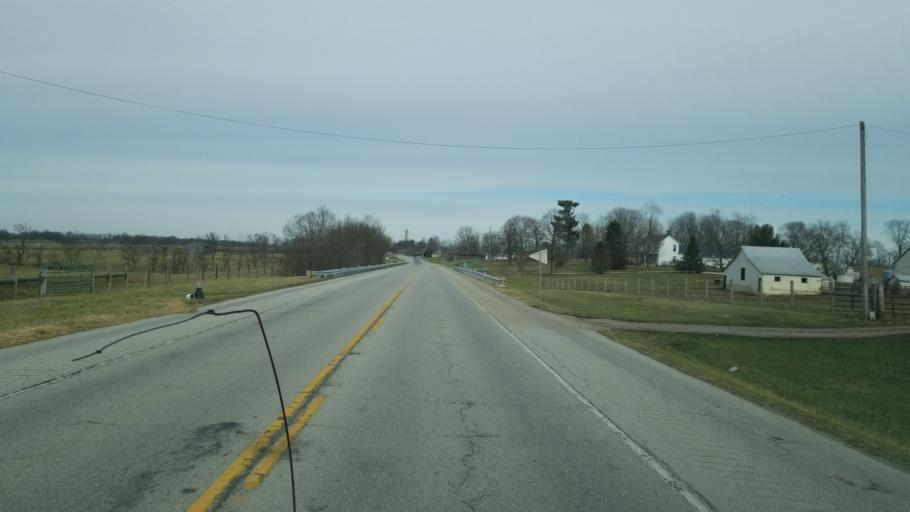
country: US
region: Kentucky
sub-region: Fleming County
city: Flemingsburg
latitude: 38.4945
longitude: -83.8549
